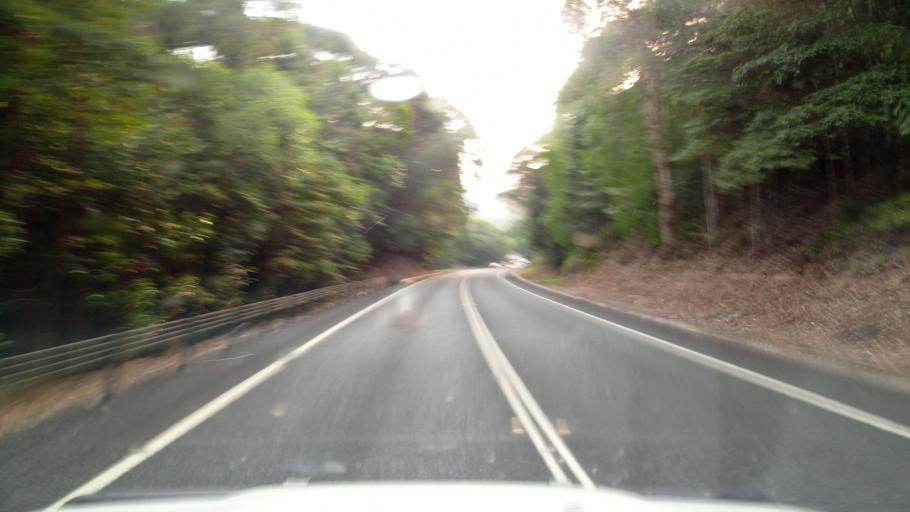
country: AU
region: Queensland
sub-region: Tablelands
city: Kuranda
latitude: -16.8449
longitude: 145.6076
